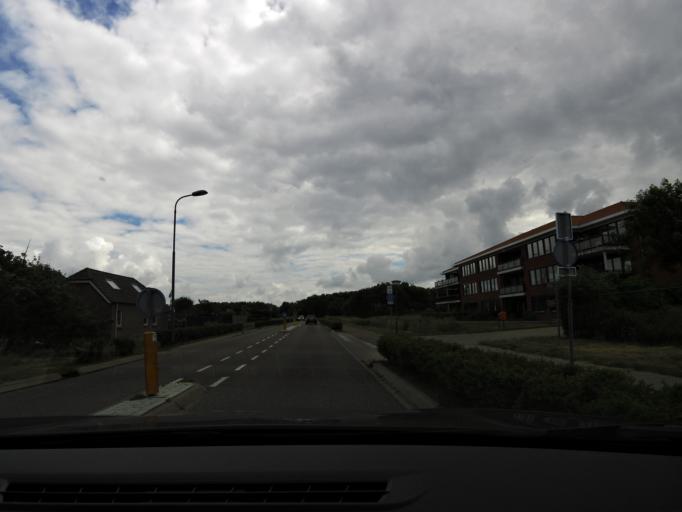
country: NL
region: Zeeland
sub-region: Gemeente Vlissingen
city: Vlissingen
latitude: 51.5268
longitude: 3.4483
